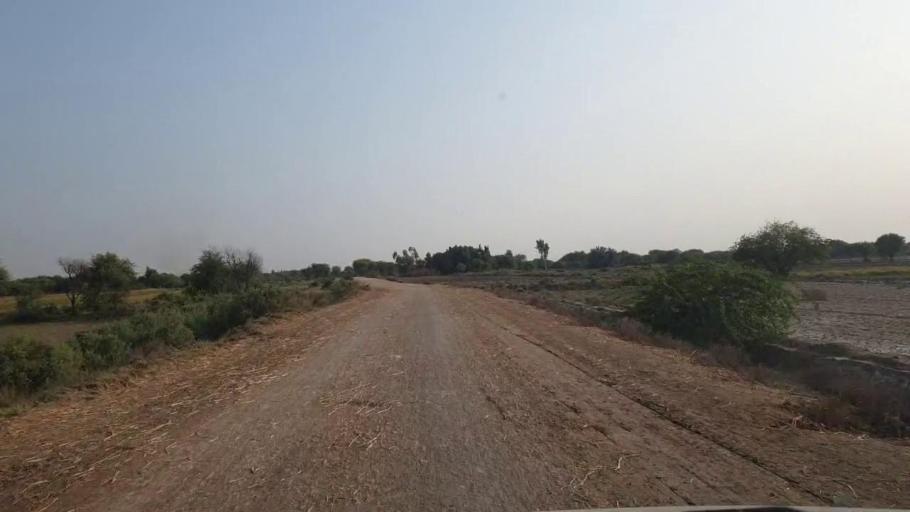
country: PK
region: Sindh
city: Rajo Khanani
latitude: 25.0408
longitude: 68.7682
